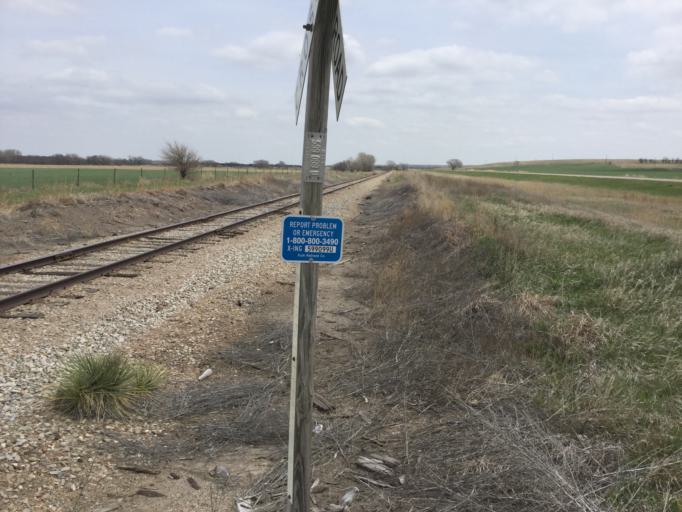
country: US
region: Kansas
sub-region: Norton County
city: Norton
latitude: 39.7675
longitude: -100.0762
